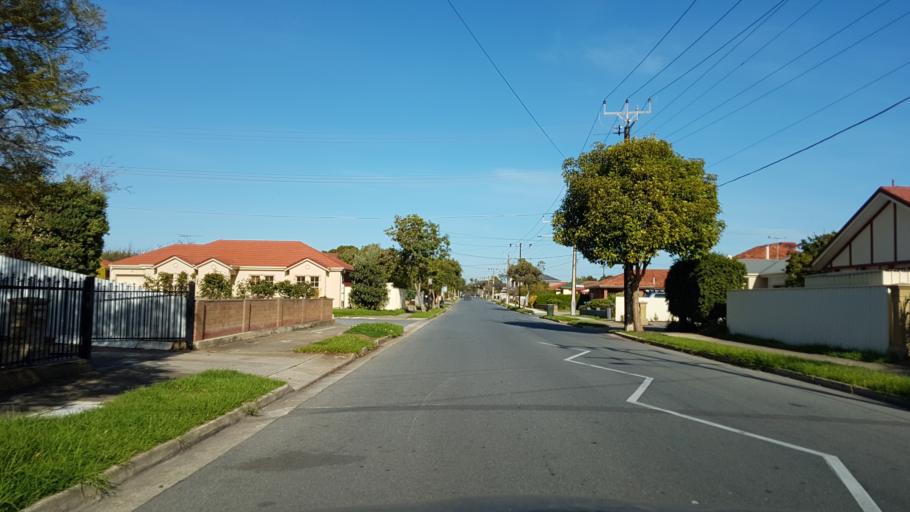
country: AU
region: South Australia
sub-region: Charles Sturt
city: Seaton
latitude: -34.8970
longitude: 138.5201
